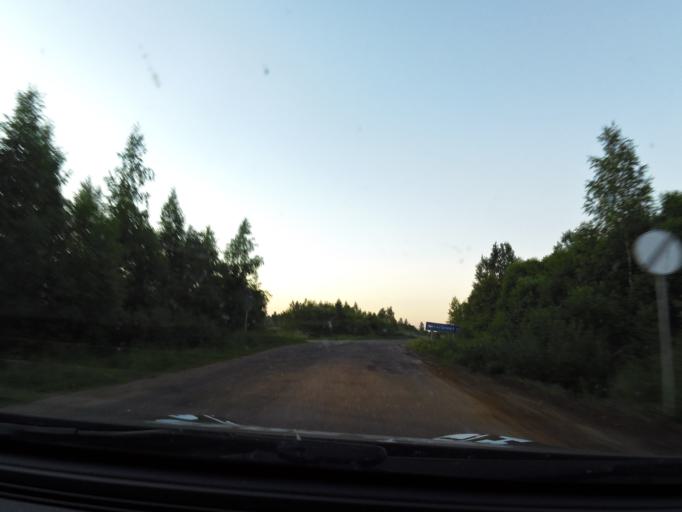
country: RU
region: Kostroma
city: Buy
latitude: 58.4490
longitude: 41.3549
